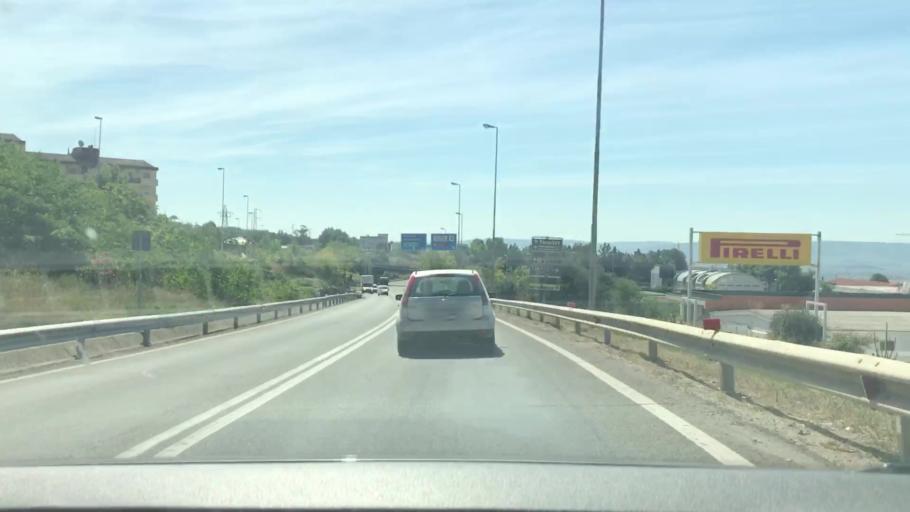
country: IT
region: Basilicate
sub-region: Provincia di Matera
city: Matera
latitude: 40.6728
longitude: 16.5776
